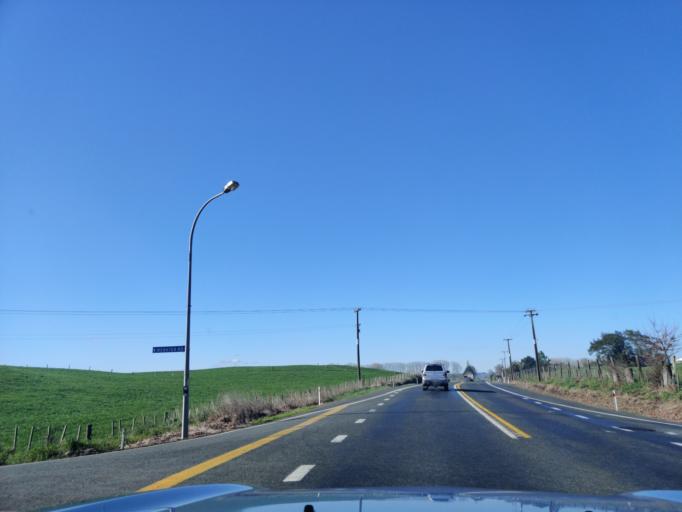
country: NZ
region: Waikato
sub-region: Matamata-Piako District
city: Matamata
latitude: -38.0122
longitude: 175.7753
